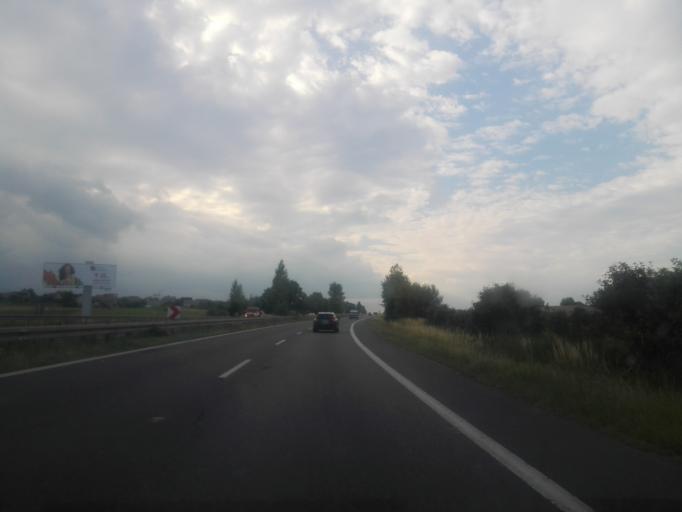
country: PL
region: Silesian Voivodeship
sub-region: Powiat bedzinski
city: Siewierz
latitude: 50.4939
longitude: 19.2054
